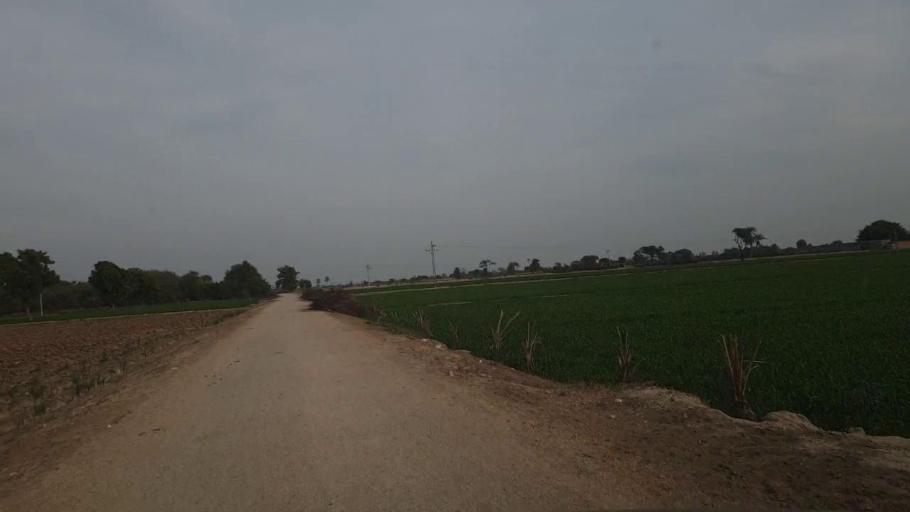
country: PK
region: Sindh
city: Shahpur Chakar
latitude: 26.1169
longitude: 68.5227
